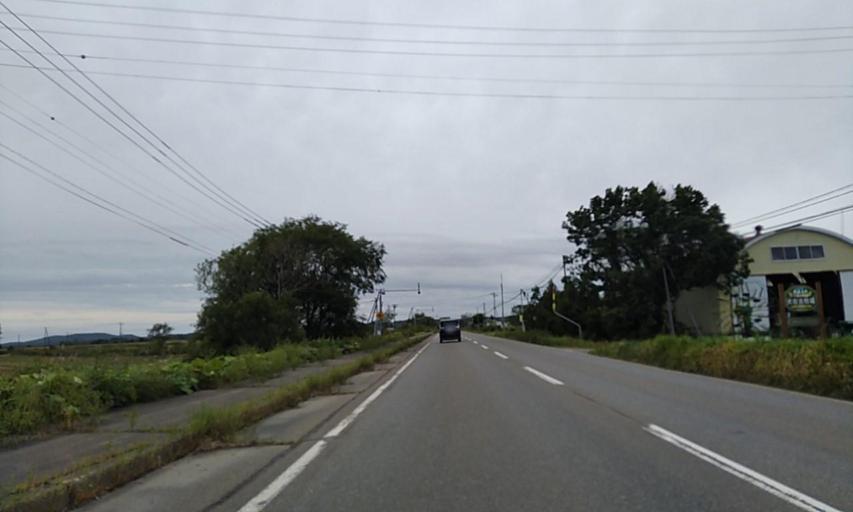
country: JP
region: Hokkaido
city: Obihiro
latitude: 42.4769
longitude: 143.2738
